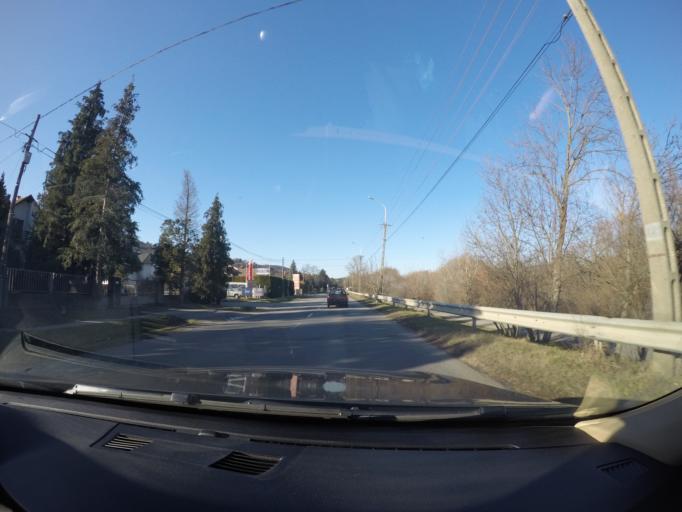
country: HU
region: Pest
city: Dunabogdany
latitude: 47.7984
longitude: 19.0238
